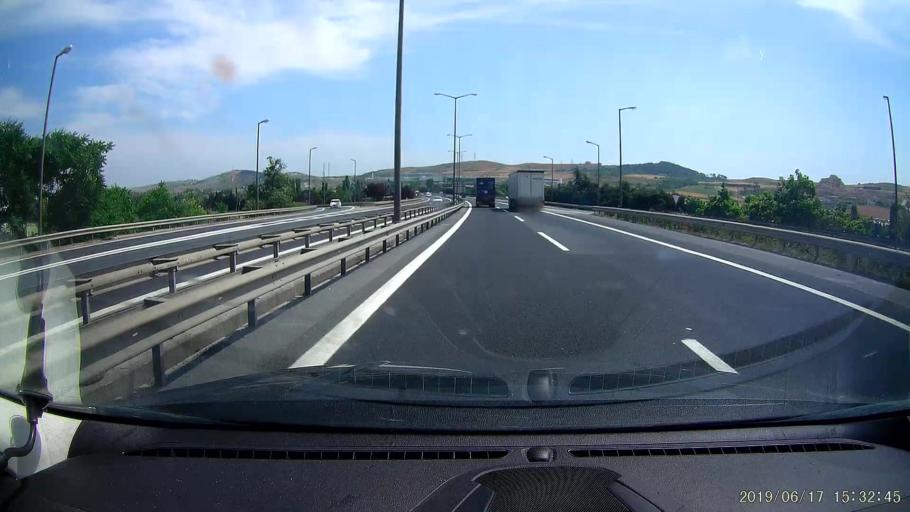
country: TR
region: Istanbul
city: Muratbey
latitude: 41.0904
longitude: 28.5093
